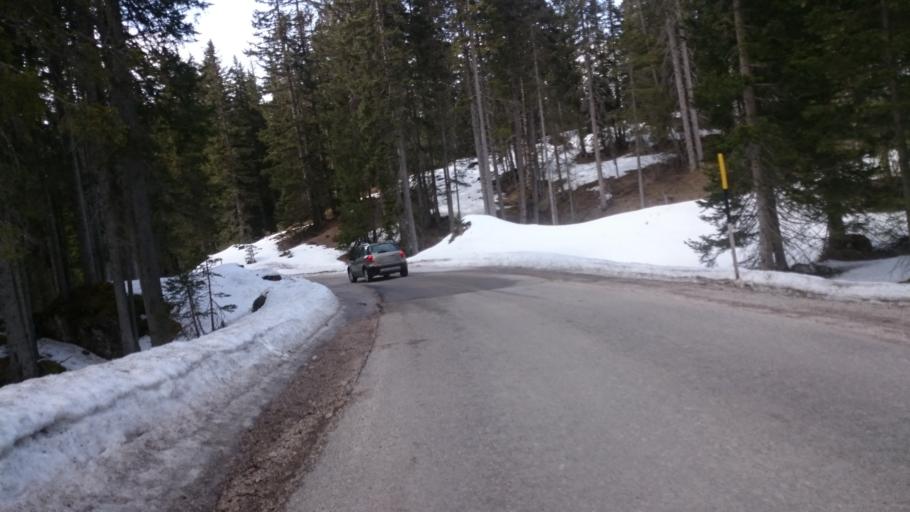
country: IT
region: Trentino-Alto Adige
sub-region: Bolzano
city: Braies
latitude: 46.6605
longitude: 12.1672
